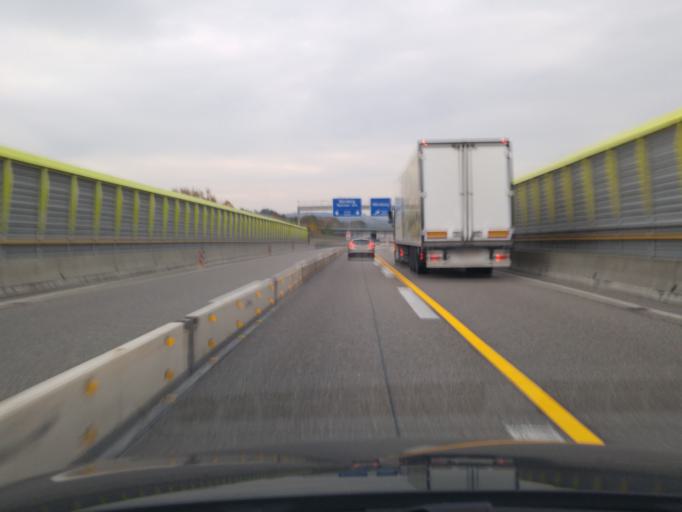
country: DE
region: Baden-Wuerttemberg
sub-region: Regierungsbezirk Stuttgart
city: Weinsberg
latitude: 49.1577
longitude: 9.2938
